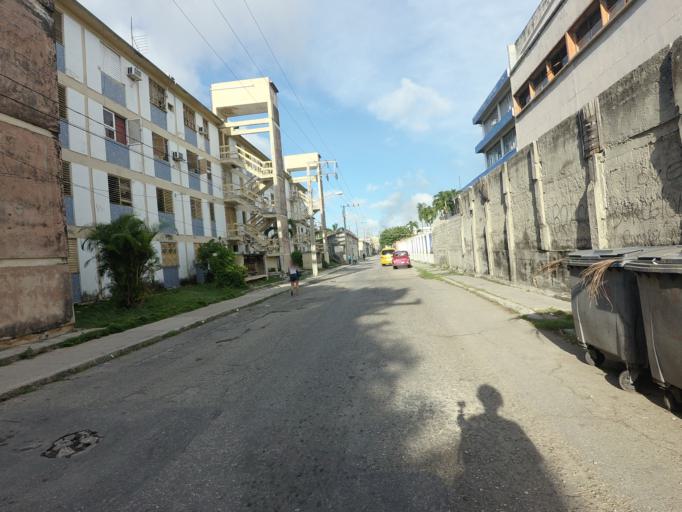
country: CU
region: La Habana
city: Havana
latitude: 23.1273
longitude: -82.3775
